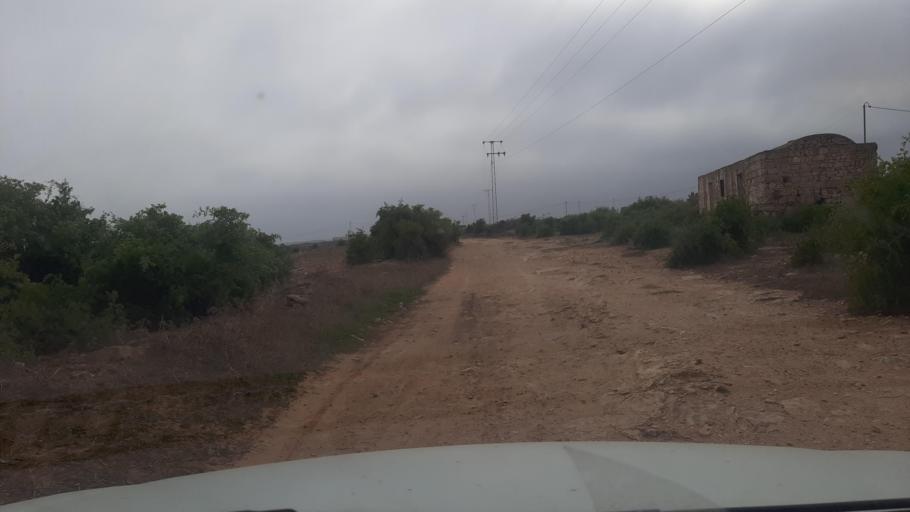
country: TN
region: Nabul
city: Menzel Heurr
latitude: 36.6895
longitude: 10.9328
